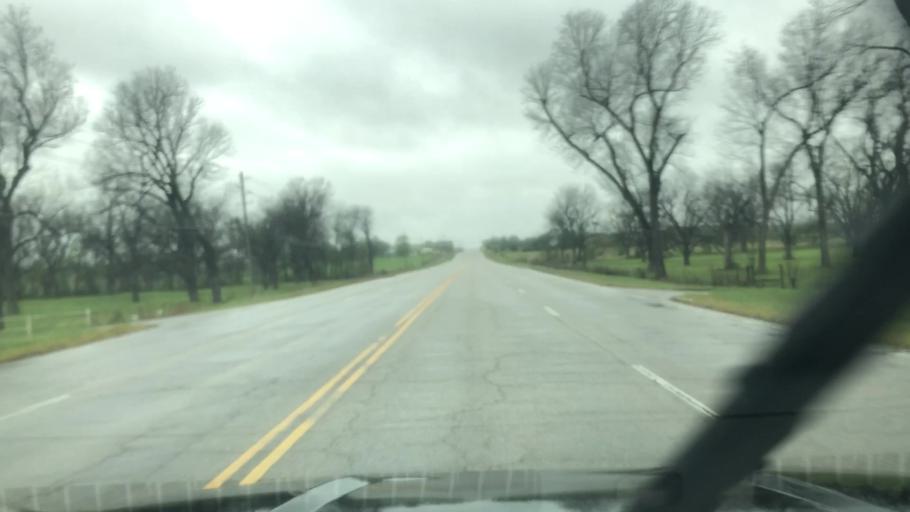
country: US
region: Oklahoma
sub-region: Tulsa County
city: Owasso
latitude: 36.2641
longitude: -95.8778
